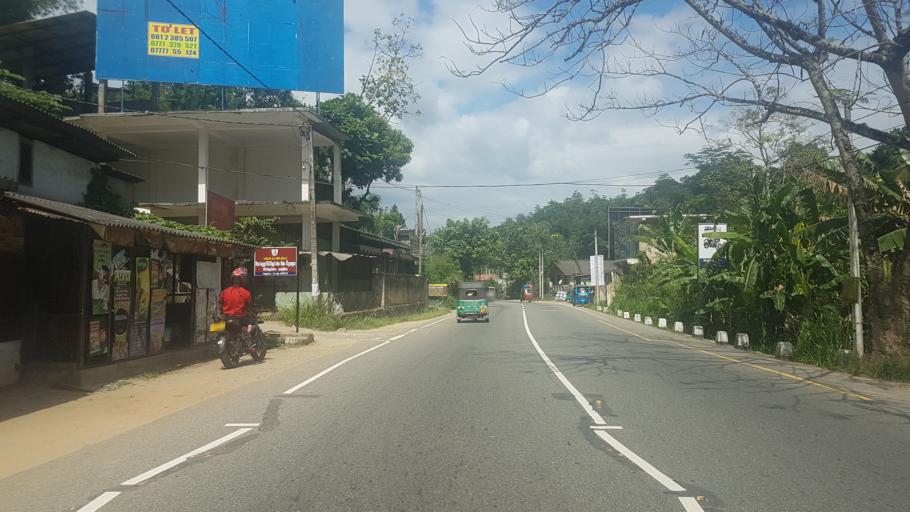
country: LK
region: Central
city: Gampola
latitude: 7.2038
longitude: 80.5993
